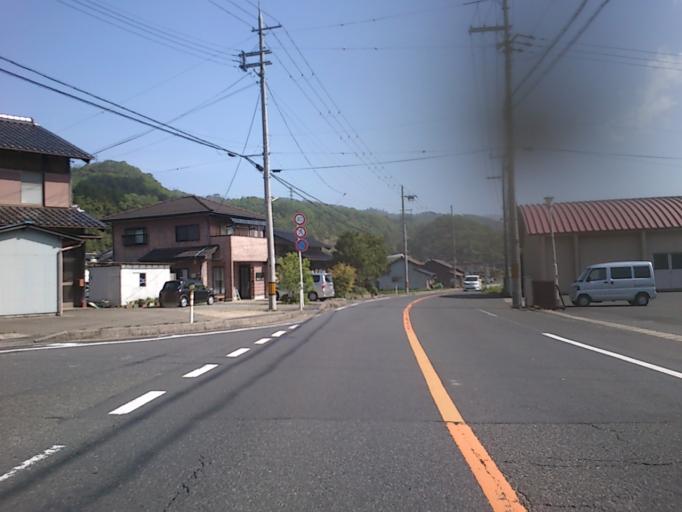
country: JP
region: Kyoto
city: Miyazu
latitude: 35.5566
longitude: 135.1393
